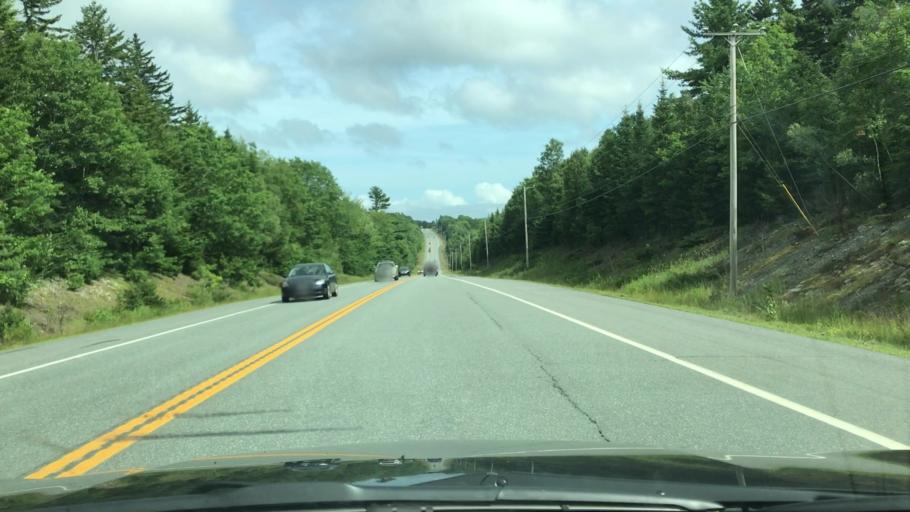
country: US
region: Maine
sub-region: Hancock County
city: Surry
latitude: 44.5524
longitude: -68.5343
